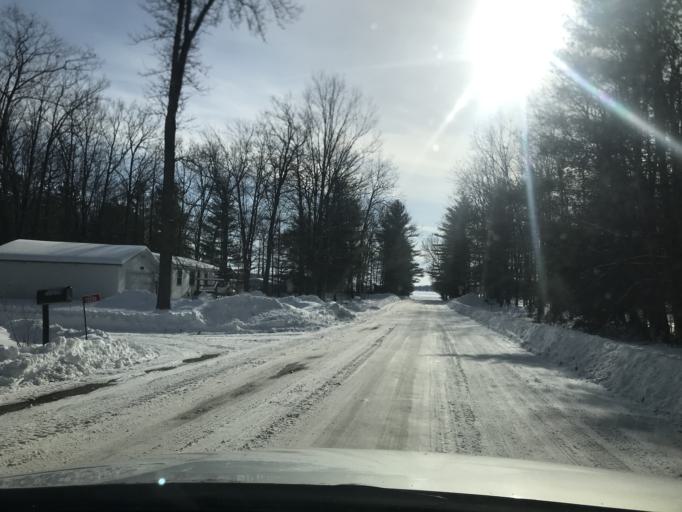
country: US
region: Wisconsin
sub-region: Oconto County
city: Gillett
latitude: 45.1543
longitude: -88.2140
